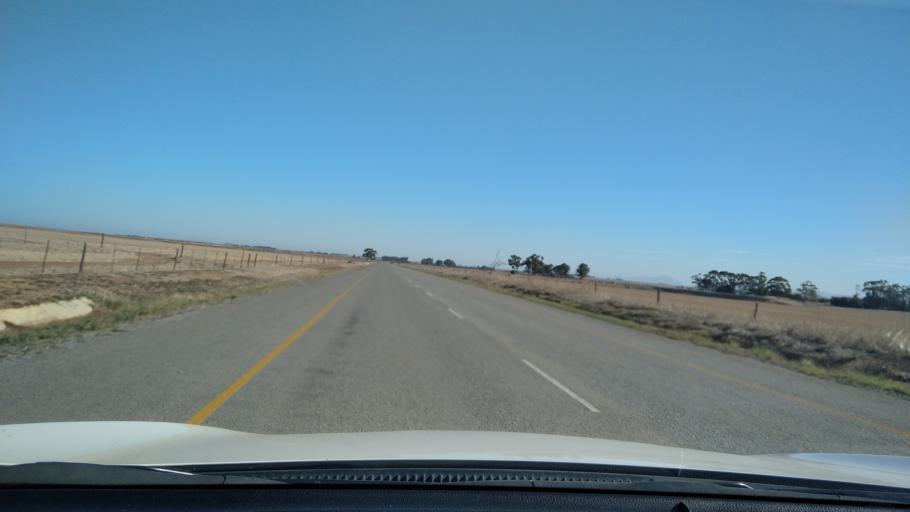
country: ZA
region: Western Cape
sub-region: West Coast District Municipality
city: Moorreesburg
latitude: -33.2911
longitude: 18.6088
